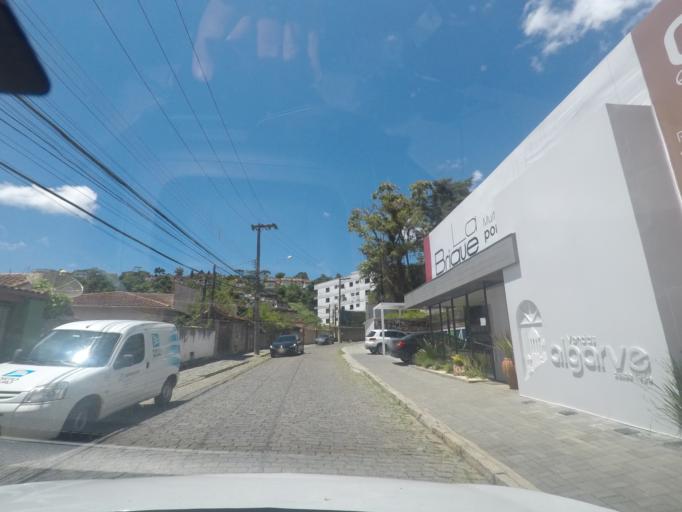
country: BR
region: Rio de Janeiro
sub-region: Teresopolis
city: Teresopolis
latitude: -22.4209
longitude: -42.9815
